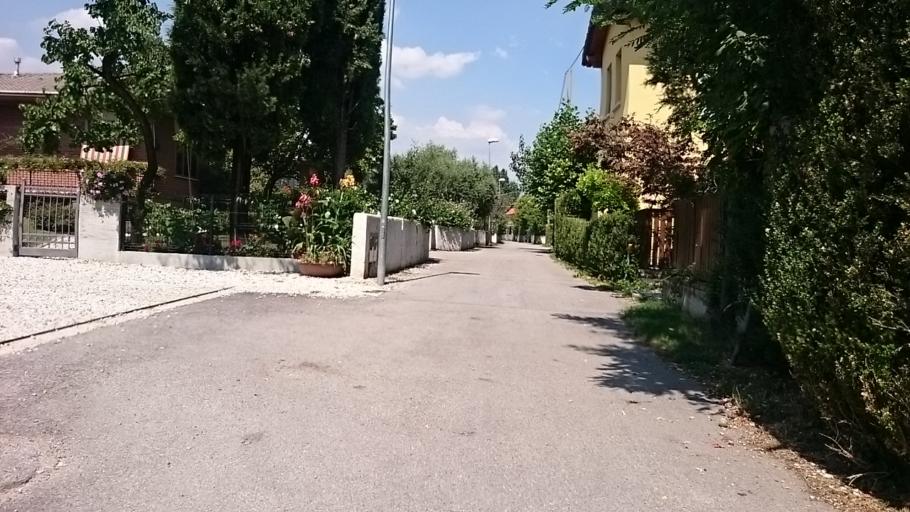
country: IT
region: Veneto
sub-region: Provincia di Vicenza
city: Rosa
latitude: 45.7193
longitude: 11.7365
